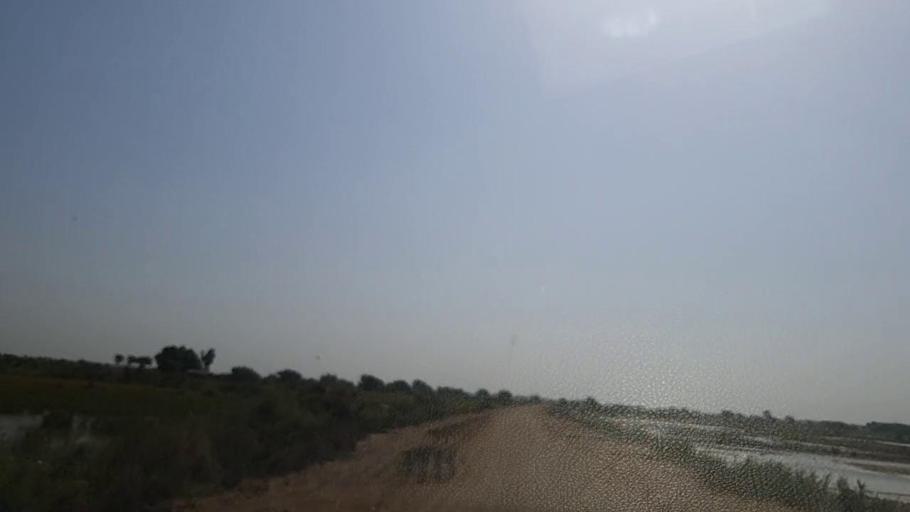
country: PK
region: Sindh
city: Daro Mehar
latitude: 24.7090
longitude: 68.1244
